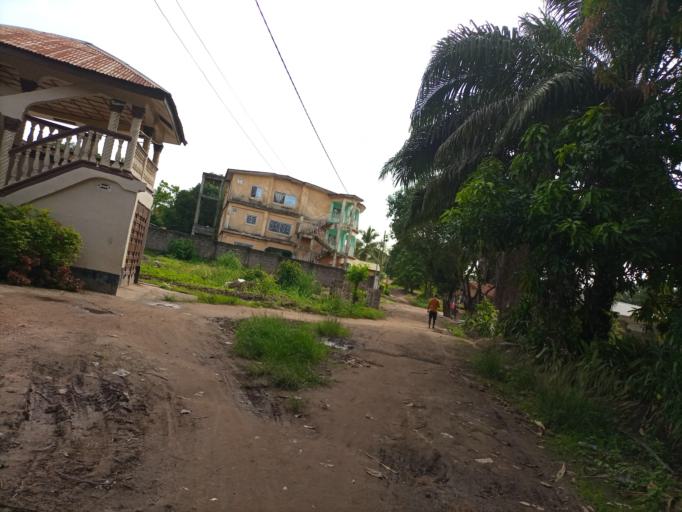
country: SL
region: Southern Province
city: Bo
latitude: 7.9633
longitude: -11.7650
